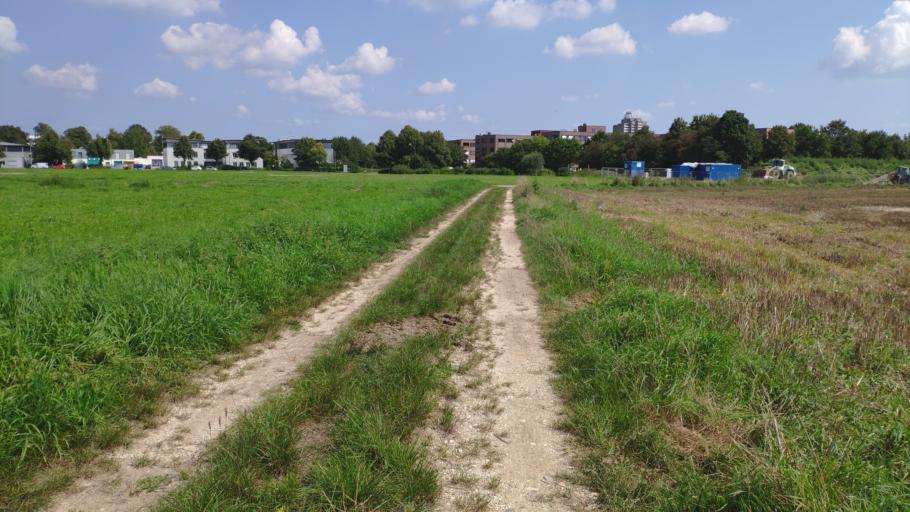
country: DE
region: Bavaria
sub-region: Swabia
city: Neu-Ulm
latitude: 48.3749
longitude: 10.0018
